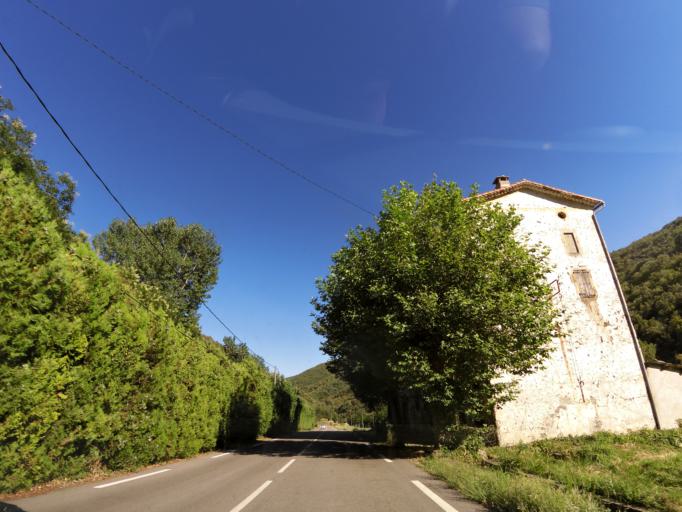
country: FR
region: Languedoc-Roussillon
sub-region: Departement du Gard
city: Valleraugue
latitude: 44.0848
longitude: 3.6166
